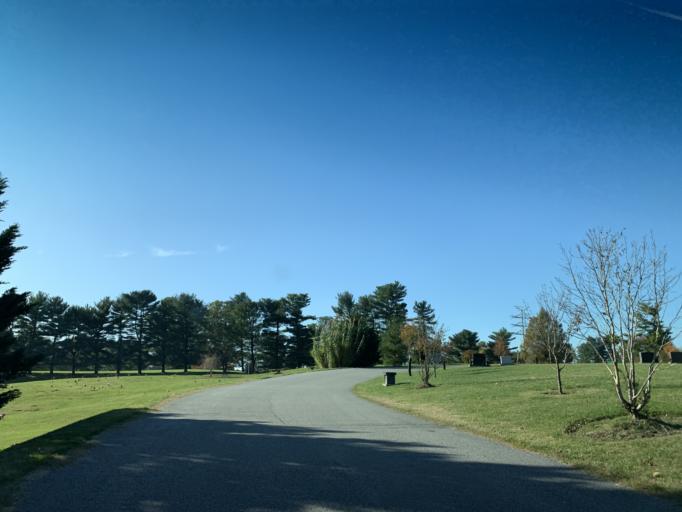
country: US
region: Maryland
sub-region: Baltimore County
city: Timonium
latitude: 39.4607
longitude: -76.6159
